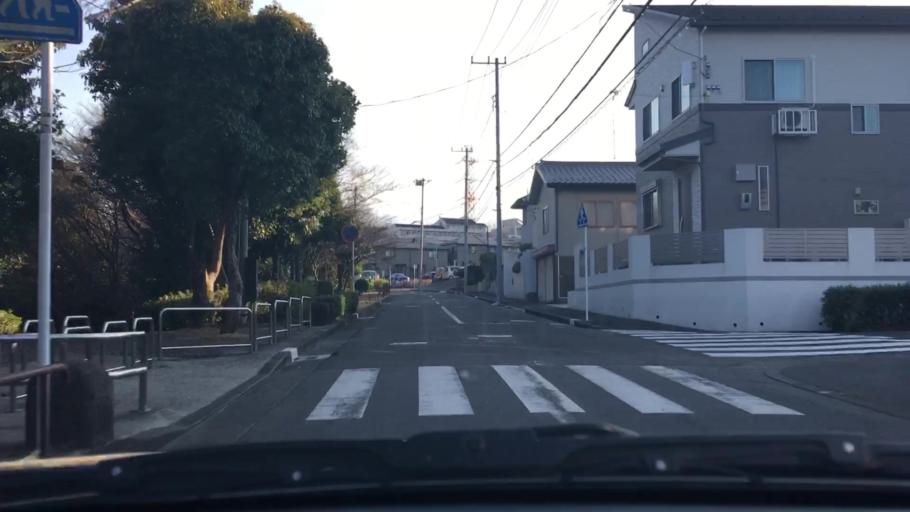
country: JP
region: Tokyo
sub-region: Machida-shi
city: Machida
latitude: 35.5422
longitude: 139.5644
